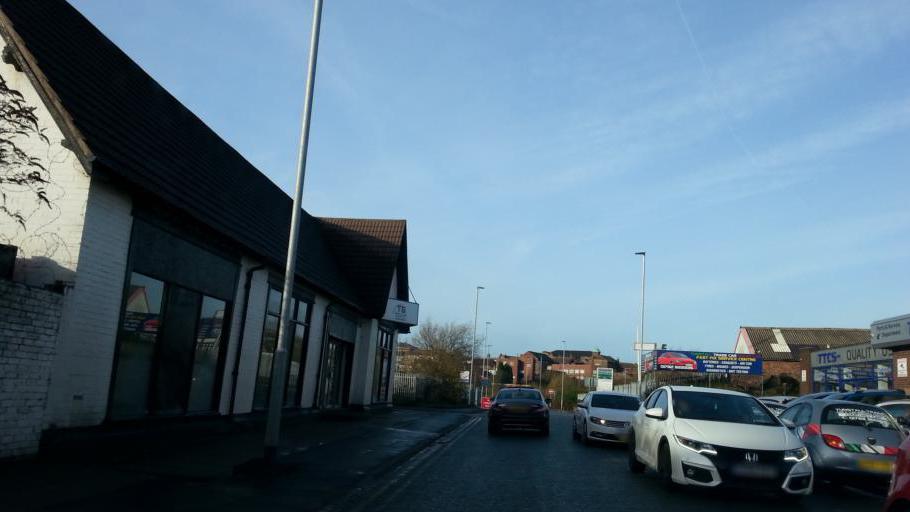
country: GB
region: England
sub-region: Stoke-on-Trent
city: Stoke-on-Trent
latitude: 53.0429
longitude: -2.1910
